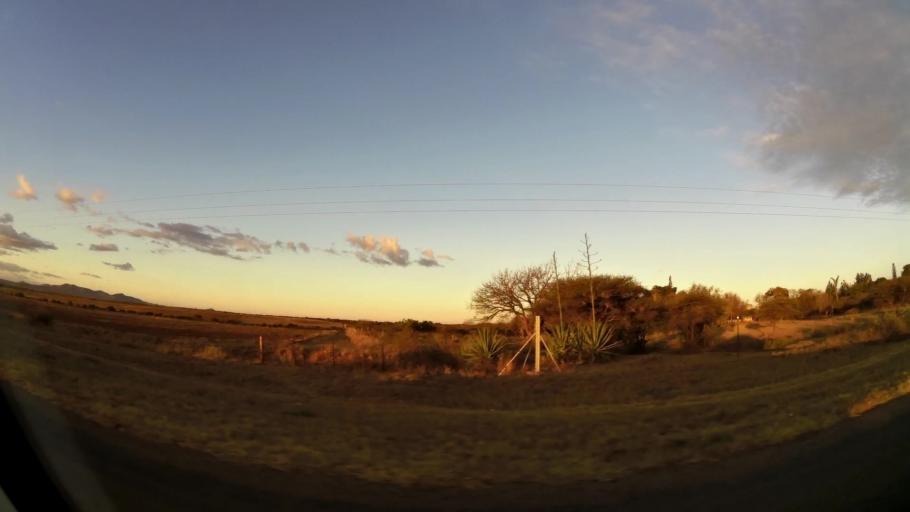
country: ZA
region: Limpopo
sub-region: Capricorn District Municipality
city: Polokwane
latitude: -23.7939
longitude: 29.4769
